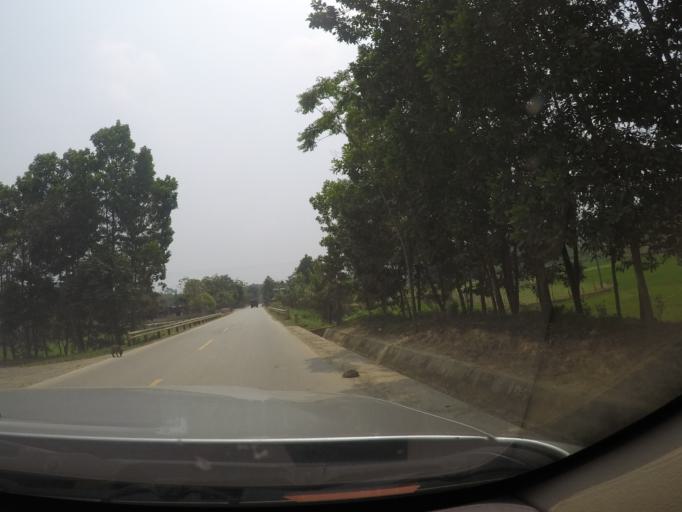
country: VN
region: Thanh Hoa
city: Thi Tran Yen Cat
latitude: 19.7360
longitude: 105.4268
